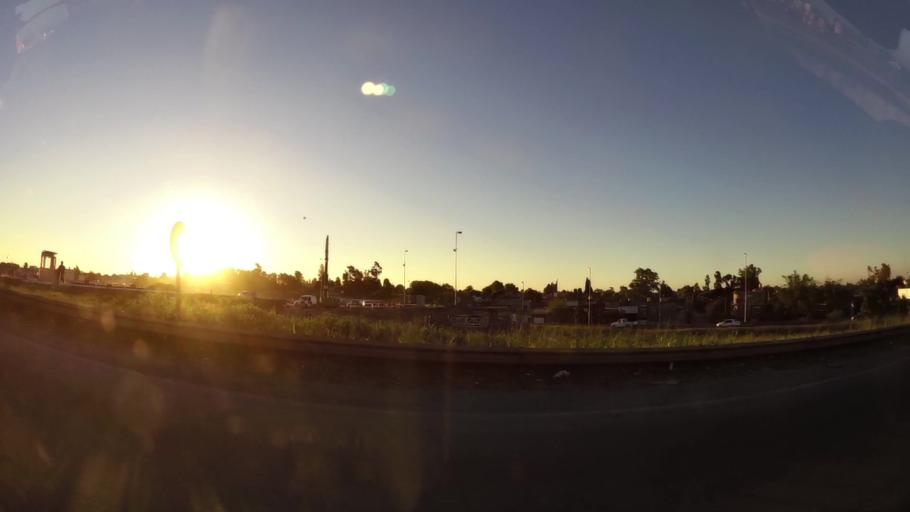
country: AR
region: Buenos Aires
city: Pontevedra
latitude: -34.7588
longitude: -58.6156
